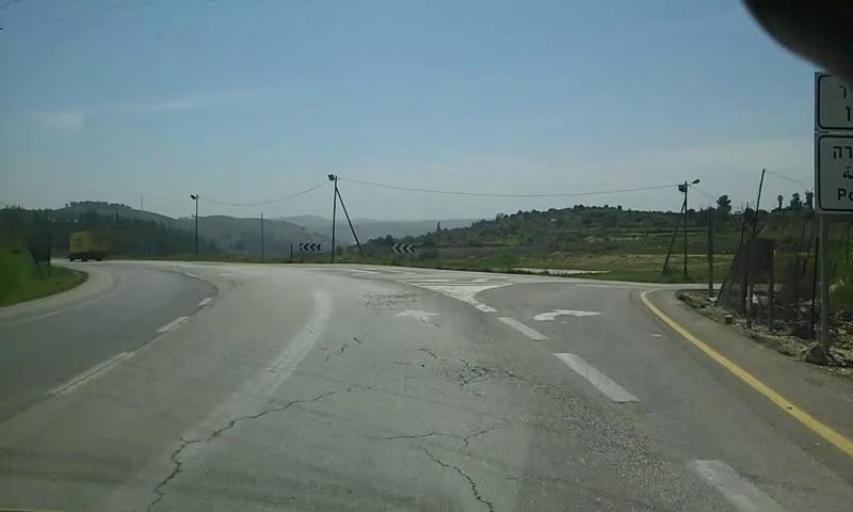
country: PS
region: West Bank
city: Nahhalin
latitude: 31.6512
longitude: 35.1255
